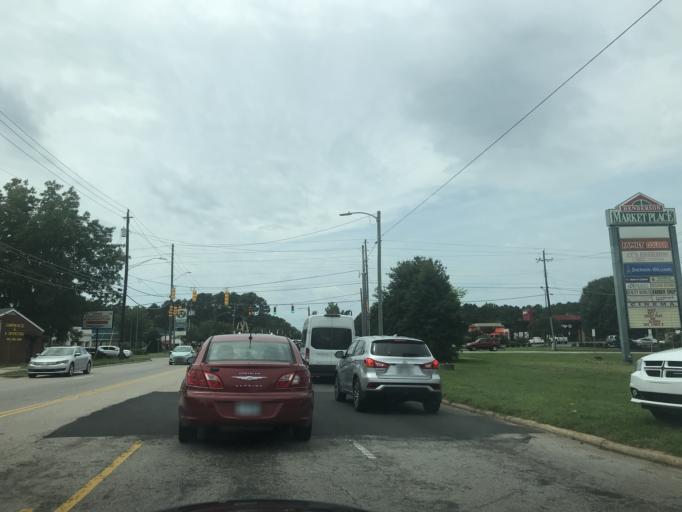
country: US
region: North Carolina
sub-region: Vance County
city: Henderson
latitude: 36.3318
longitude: -78.4337
